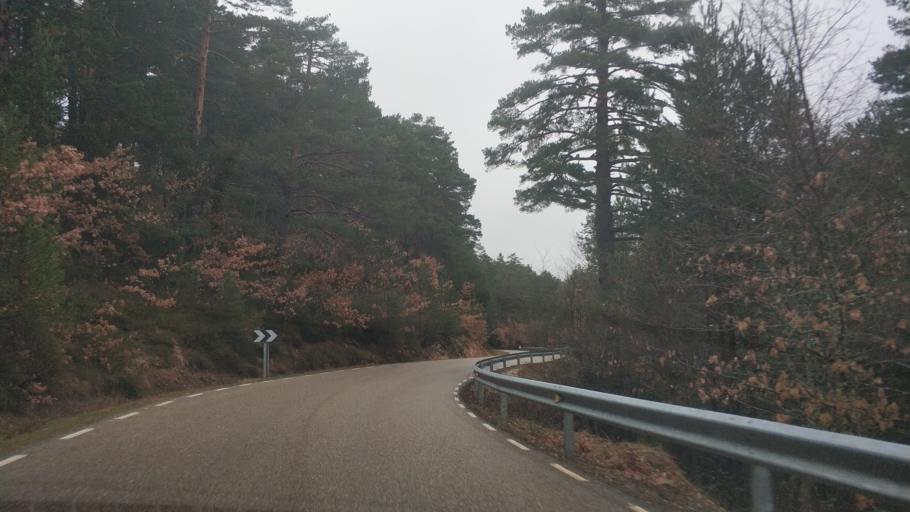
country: ES
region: Castille and Leon
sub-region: Provincia de Burgos
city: Quintanar de la Sierra
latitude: 42.0057
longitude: -3.0201
